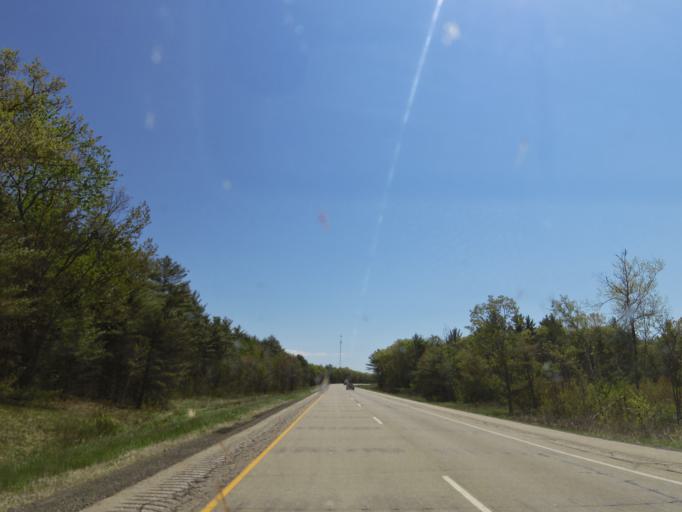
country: US
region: Wisconsin
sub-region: Monroe County
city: Tomah
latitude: 44.1543
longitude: -90.5595
